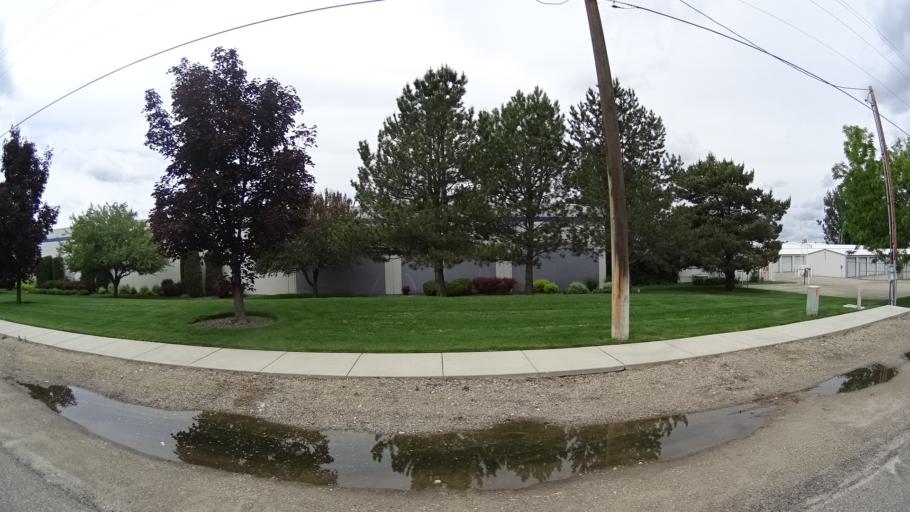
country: US
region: Idaho
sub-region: Ada County
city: Eagle
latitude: 43.6884
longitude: -116.3140
